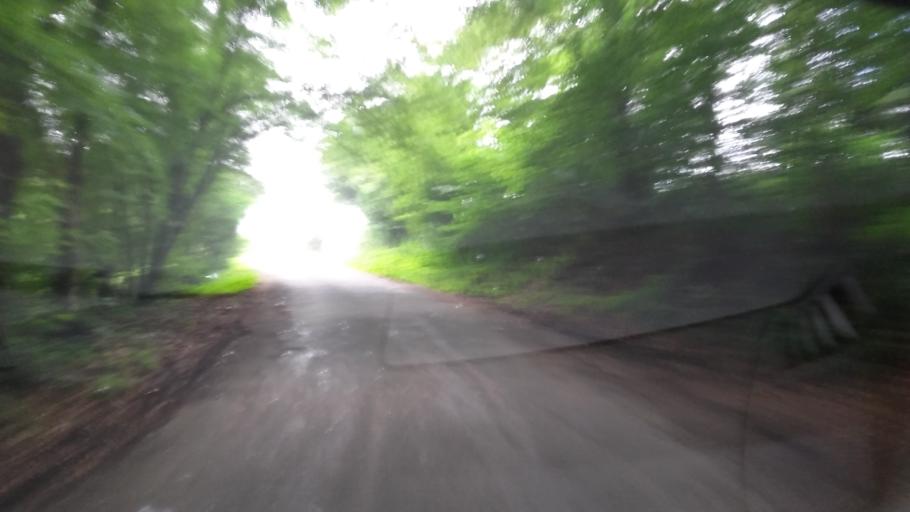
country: LU
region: Luxembourg
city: Eischen
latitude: 49.6685
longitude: 5.8552
